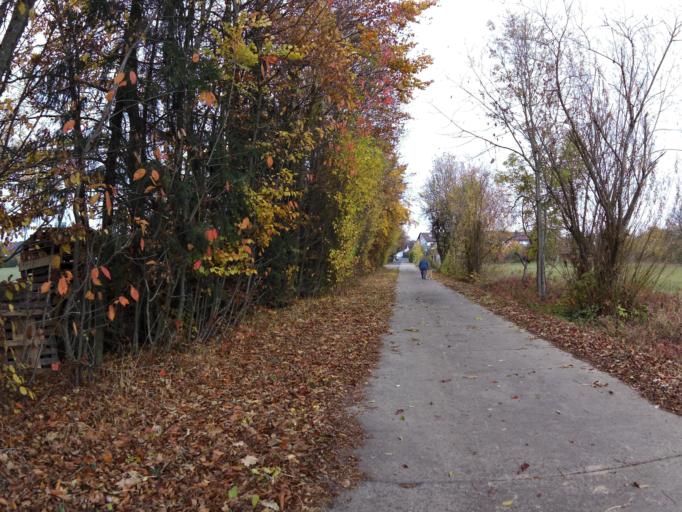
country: DE
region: Bavaria
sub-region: Regierungsbezirk Unterfranken
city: Kist
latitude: 49.7396
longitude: 9.8369
